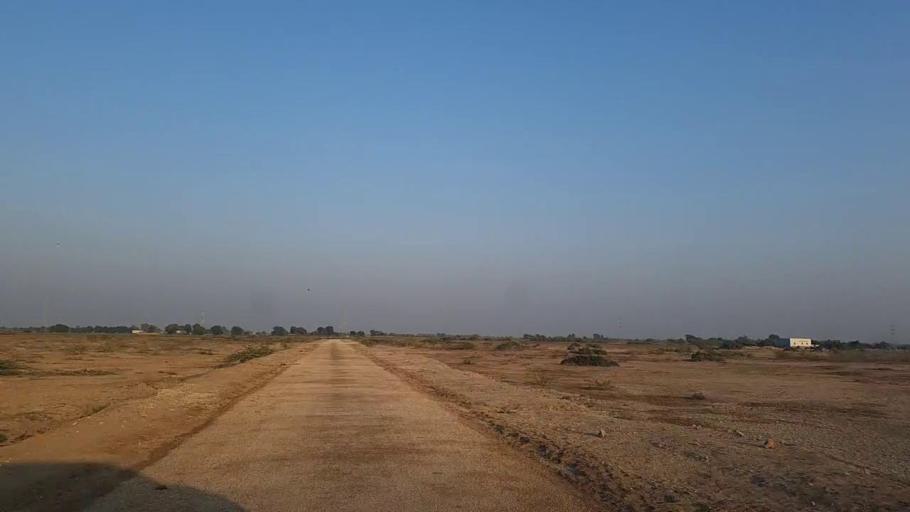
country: PK
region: Sindh
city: Naukot
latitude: 24.9718
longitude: 69.4667
